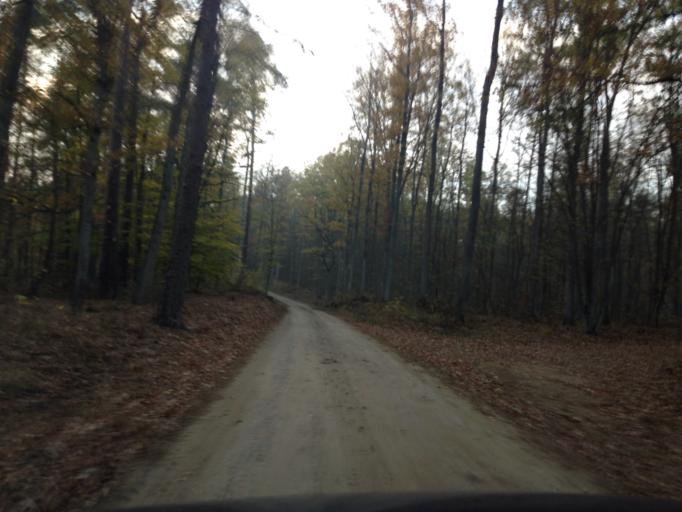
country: PL
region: Warmian-Masurian Voivodeship
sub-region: Powiat dzialdowski
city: Lidzbark
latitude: 53.2688
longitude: 19.7354
